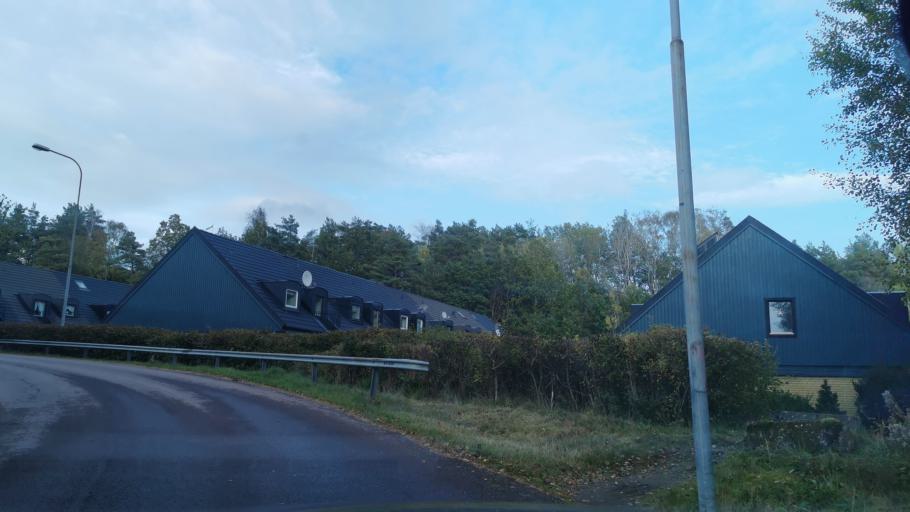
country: SE
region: Vaestra Goetaland
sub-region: Partille Kommun
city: Partille
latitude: 57.7158
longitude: 12.0820
